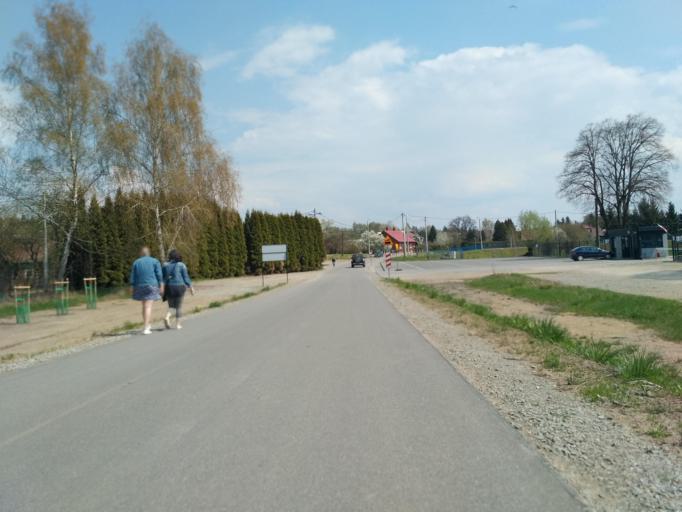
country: PL
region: Subcarpathian Voivodeship
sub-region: Powiat krosnienski
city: Jedlicze
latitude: 49.7270
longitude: 21.6239
